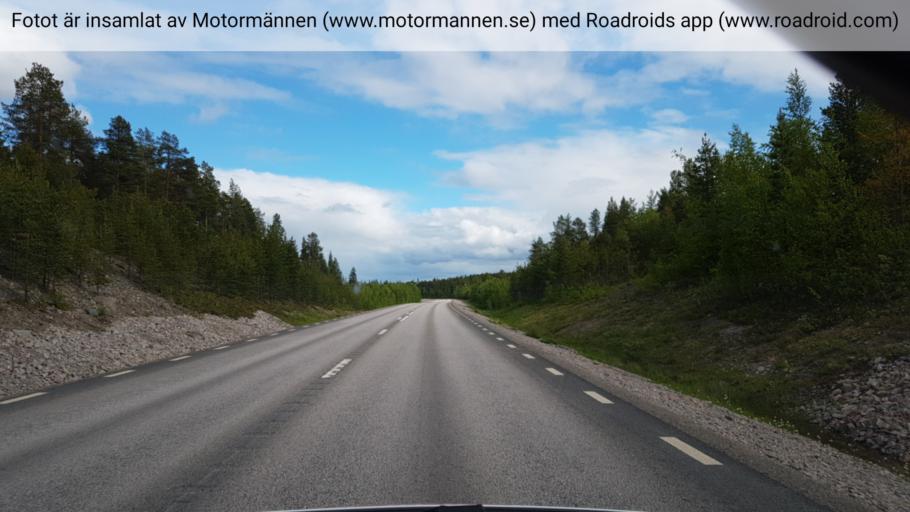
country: SE
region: Norrbotten
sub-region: Gallivare Kommun
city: Malmberget
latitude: 67.6656
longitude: 21.4242
